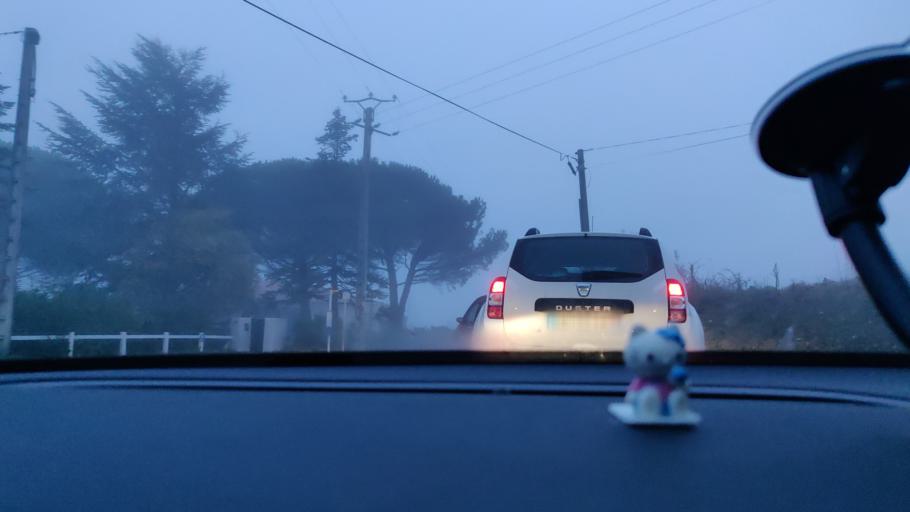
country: FR
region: Midi-Pyrenees
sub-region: Departement de la Haute-Garonne
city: Vieille-Toulouse
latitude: 43.4951
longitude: 1.4539
